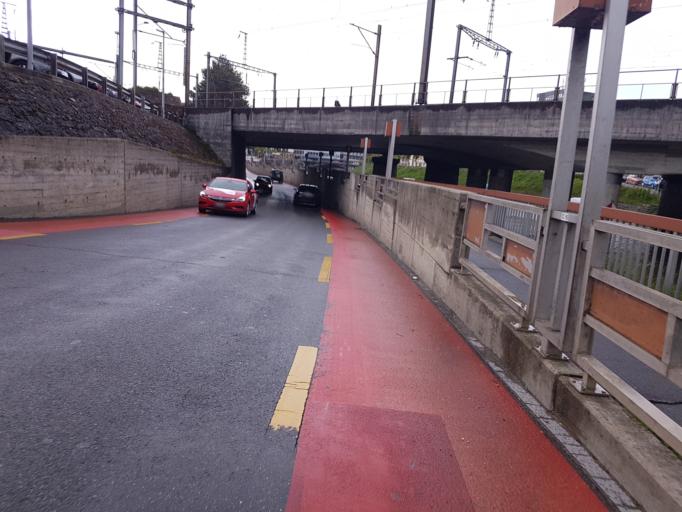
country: CH
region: Vaud
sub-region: Jura-Nord vaudois District
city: Yverdon-les-Bains
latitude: 46.7832
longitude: 6.6372
